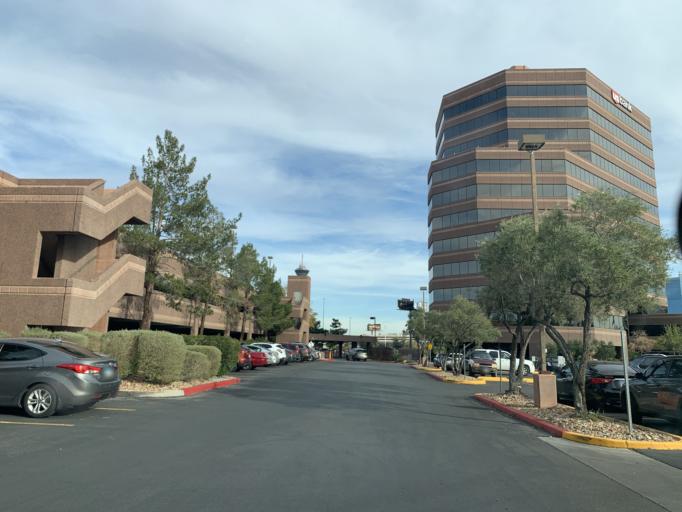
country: US
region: Nevada
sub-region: Clark County
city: Las Vegas
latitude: 36.1452
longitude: -115.1749
